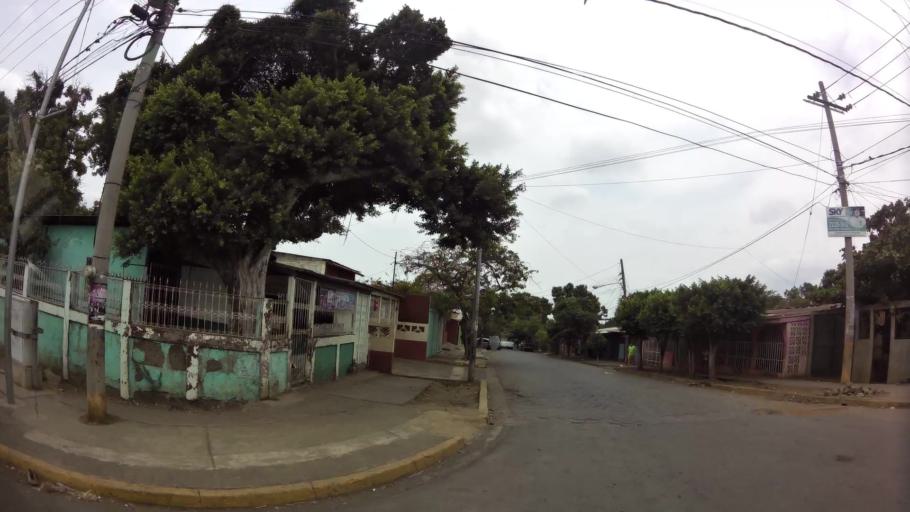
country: NI
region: Managua
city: Managua
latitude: 12.1094
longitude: -86.2237
